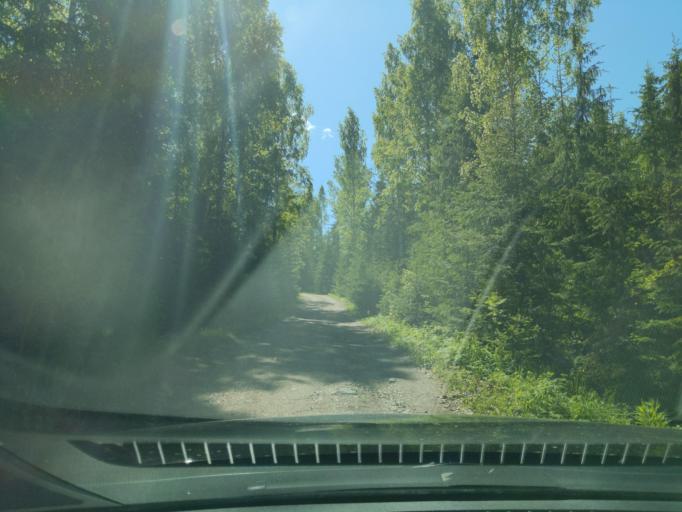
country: FI
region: Paijanne Tavastia
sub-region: Lahti
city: Lahti
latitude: 61.0537
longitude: 25.6959
